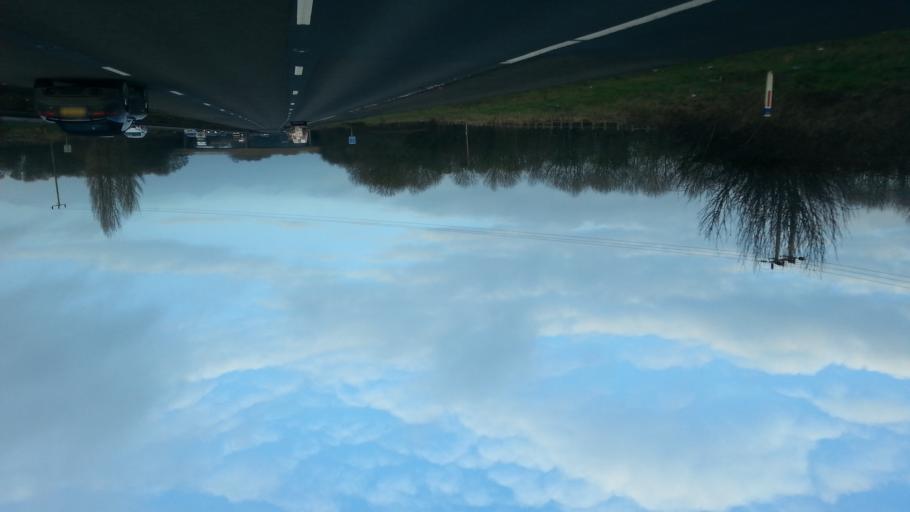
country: GB
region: England
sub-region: Gloucestershire
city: Dursley
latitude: 51.7063
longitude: -2.3849
